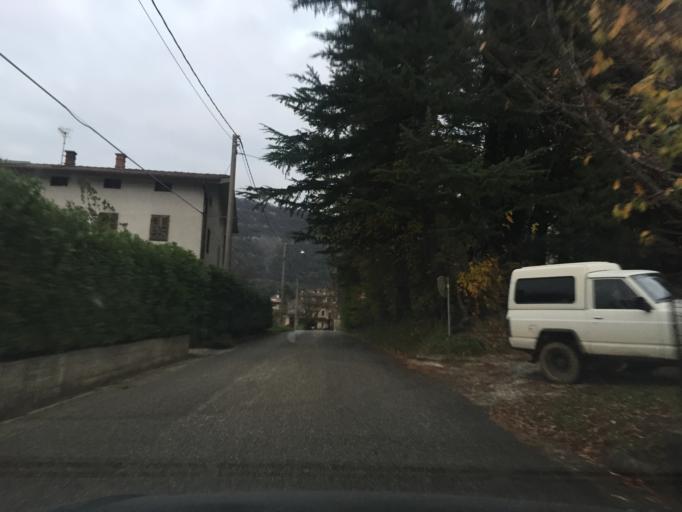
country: SI
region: Nova Gorica
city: Solkan
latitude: 45.9748
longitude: 13.6263
